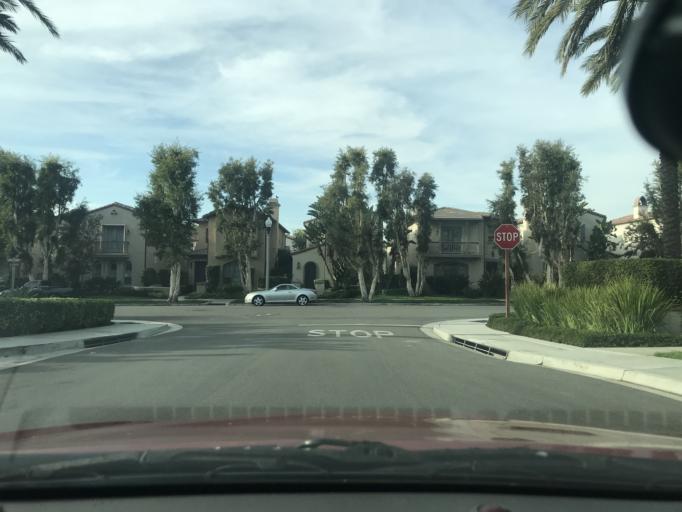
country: US
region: California
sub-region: Orange County
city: Irvine
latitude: 33.6965
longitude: -117.7537
